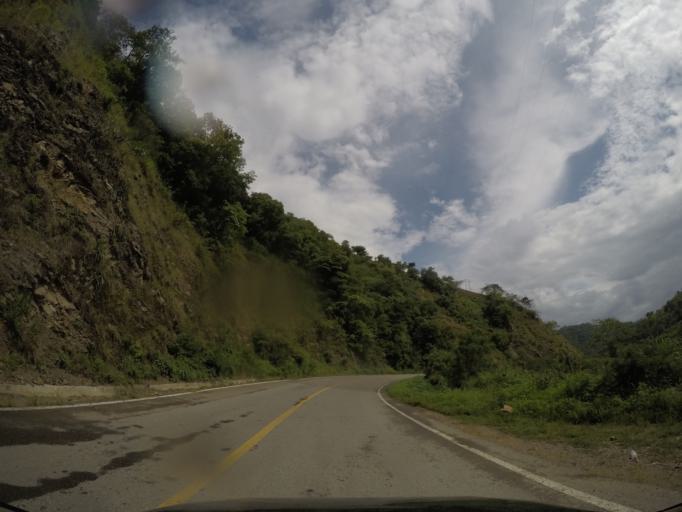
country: MX
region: Oaxaca
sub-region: San Jeronimo Coatlan
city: San Cristobal Honduras
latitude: 16.3834
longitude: -97.0759
